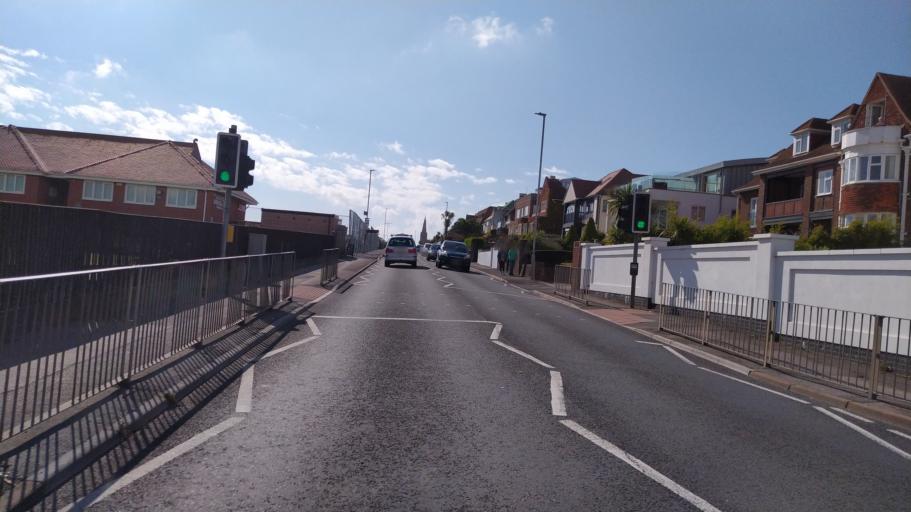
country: GB
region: England
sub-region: Dorset
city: Weymouth
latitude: 50.6229
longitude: -2.4464
